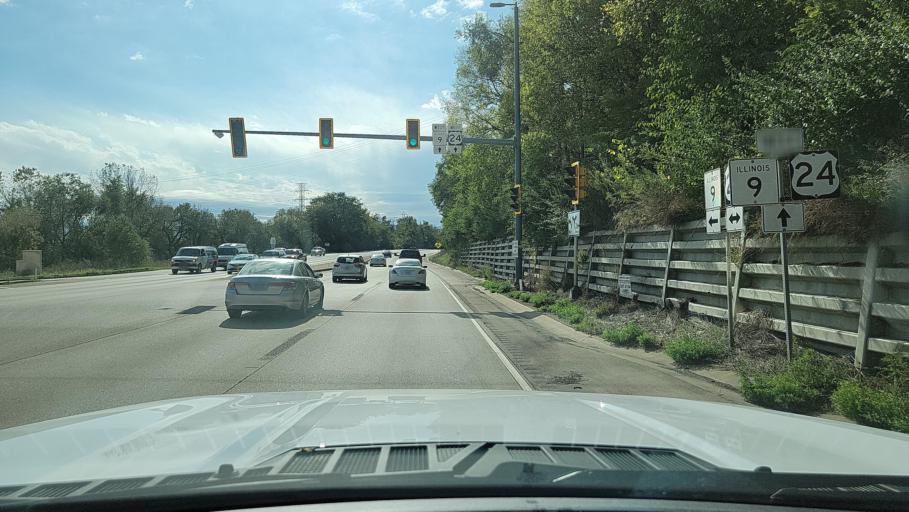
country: US
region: Illinois
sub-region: Tazewell County
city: Pekin
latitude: 40.5897
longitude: -89.6784
